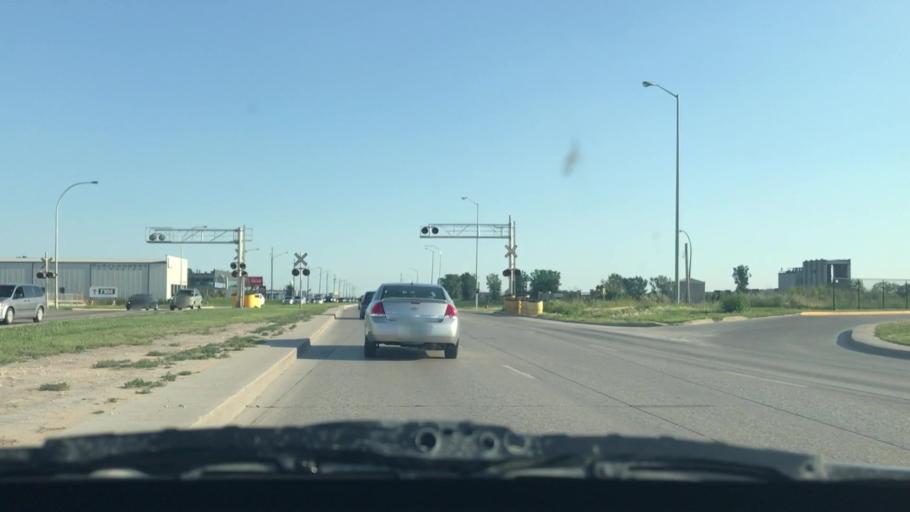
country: CA
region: Manitoba
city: Winnipeg
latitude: 49.8388
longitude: -97.2092
